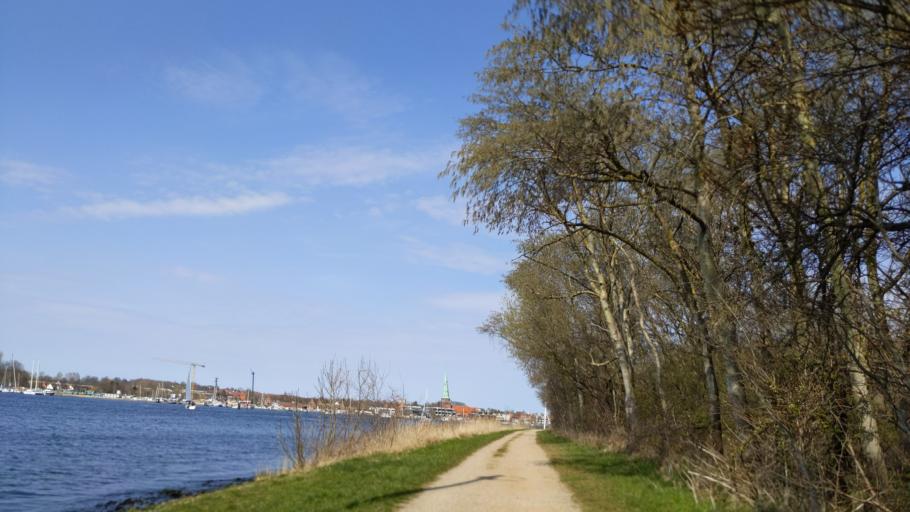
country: DE
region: Schleswig-Holstein
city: Travemuende
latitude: 53.9489
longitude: 10.8632
